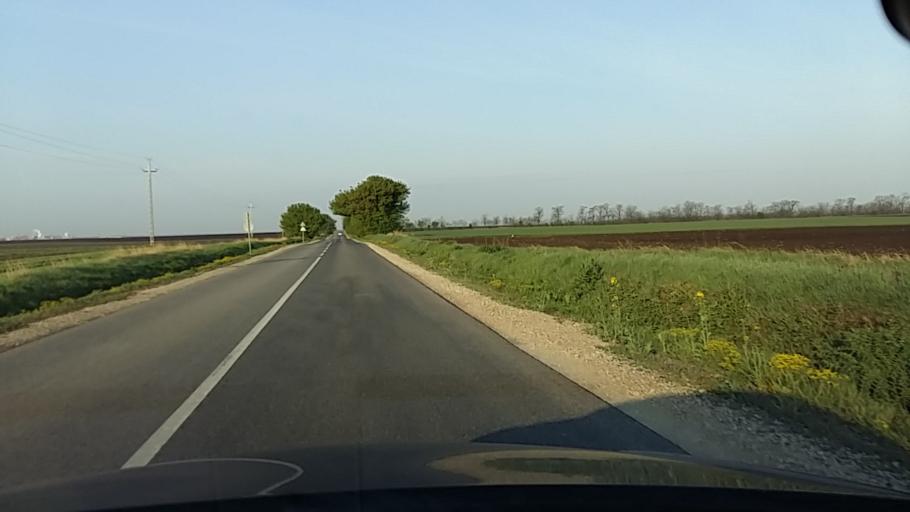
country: HU
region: Fejer
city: Pusztaszabolcs
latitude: 47.1103
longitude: 18.7503
